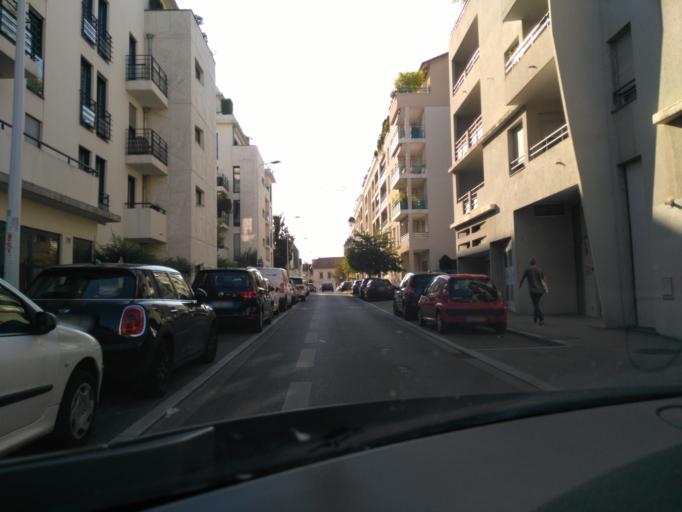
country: FR
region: Rhone-Alpes
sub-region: Departement du Rhone
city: Lyon
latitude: 45.7417
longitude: 4.8711
